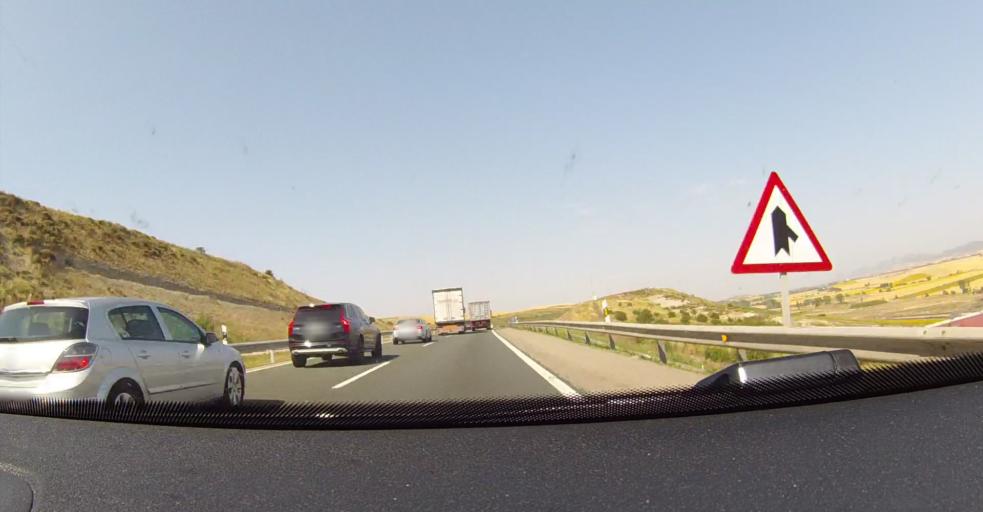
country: ES
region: Castille and Leon
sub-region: Provincia de Burgos
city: Pancorbo
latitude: 42.6223
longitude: -3.1173
